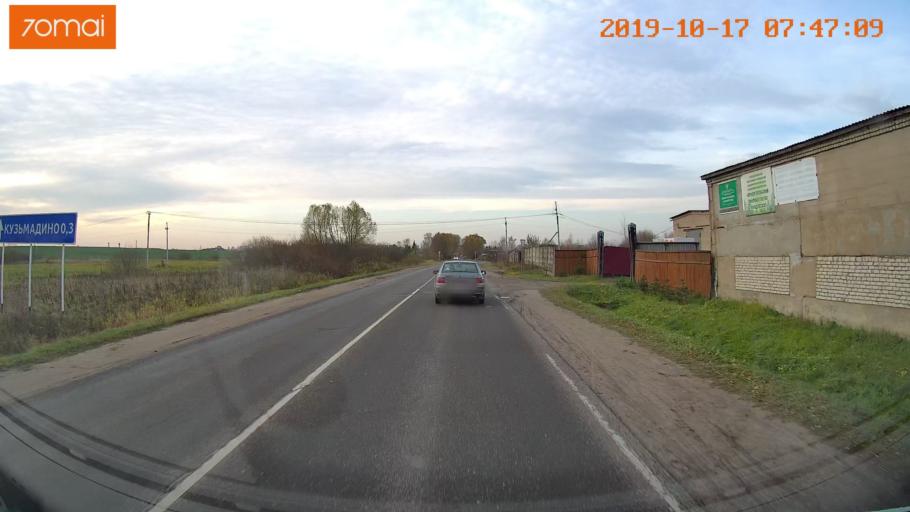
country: RU
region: Vladimir
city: Yur'yev-Pol'skiy
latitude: 56.4892
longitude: 39.6872
